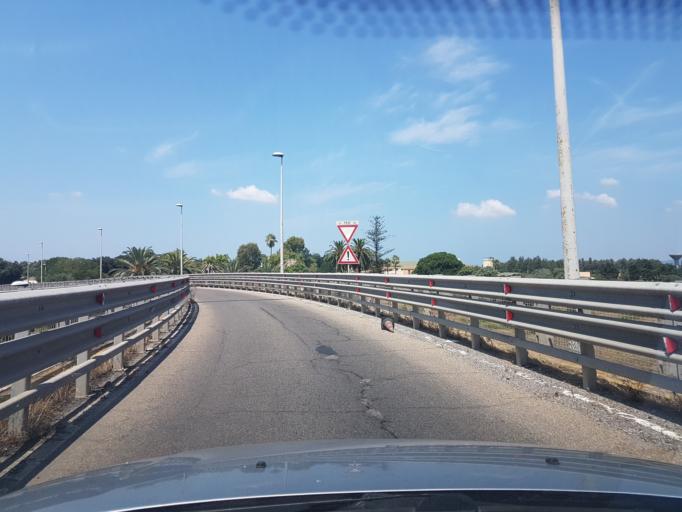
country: IT
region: Sardinia
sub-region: Provincia di Oristano
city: Donigala Fenugheddu
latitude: 39.9272
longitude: 8.5788
